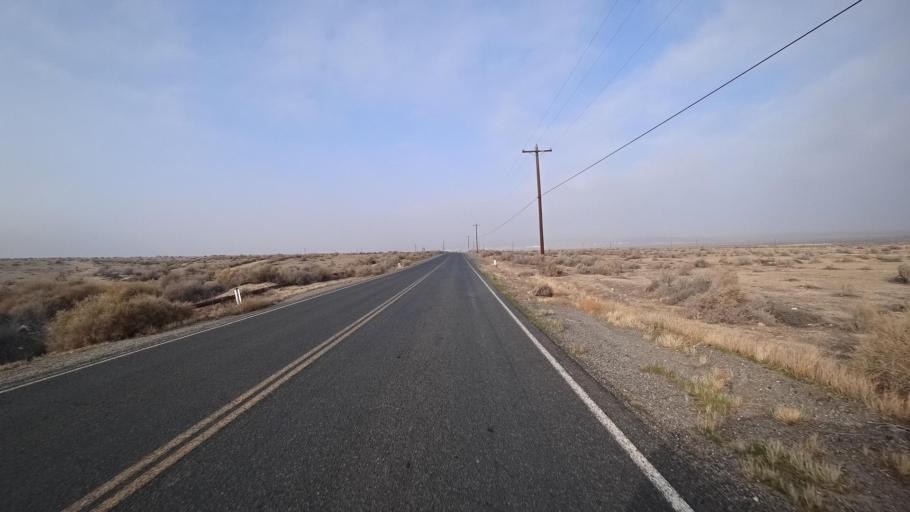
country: US
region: California
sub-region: Kern County
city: Ford City
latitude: 35.2063
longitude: -119.4457
